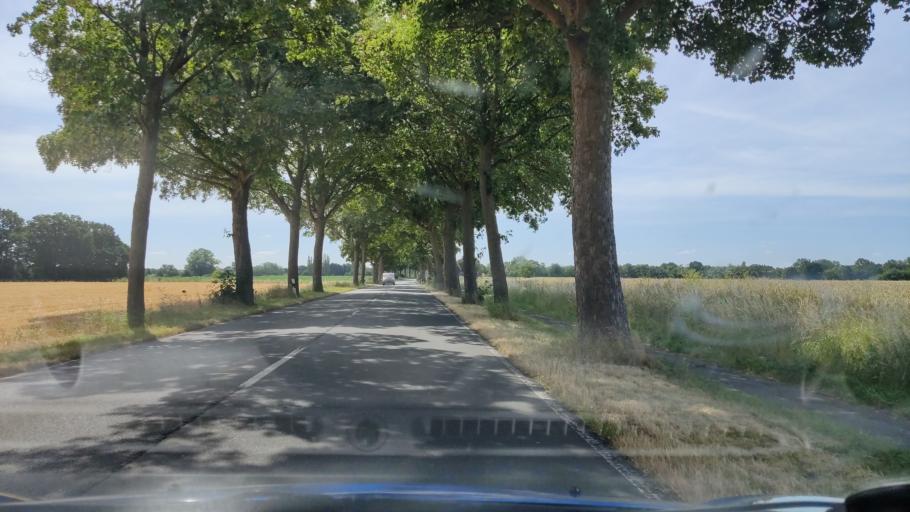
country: DE
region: Lower Saxony
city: Neustadt am Rubenberge
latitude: 52.5238
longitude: 9.4642
